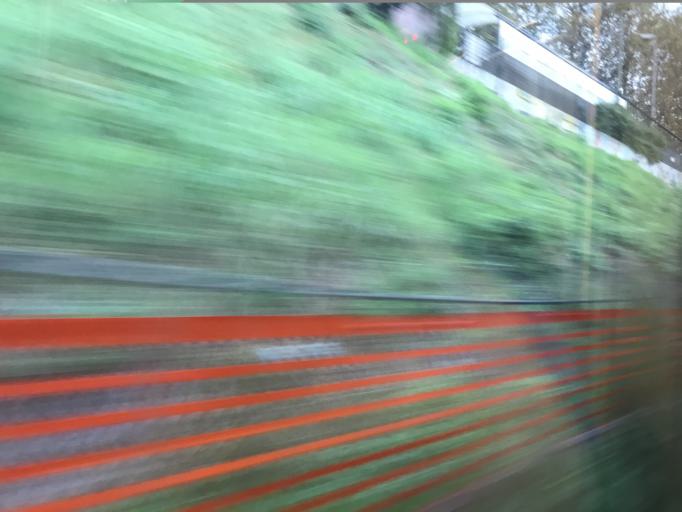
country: IT
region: Latium
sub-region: Citta metropolitana di Roma Capitale
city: Rome
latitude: 41.8717
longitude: 12.4922
